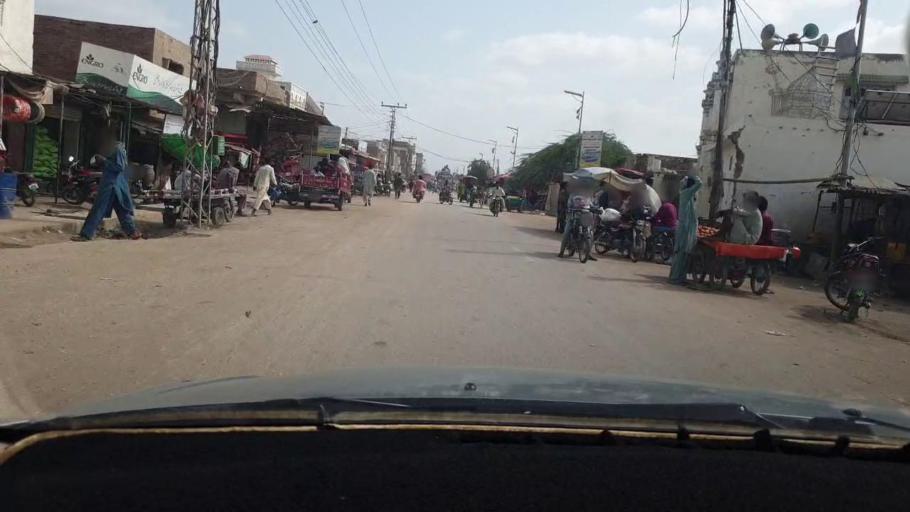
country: PK
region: Sindh
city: Naukot
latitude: 24.9688
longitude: 69.2977
